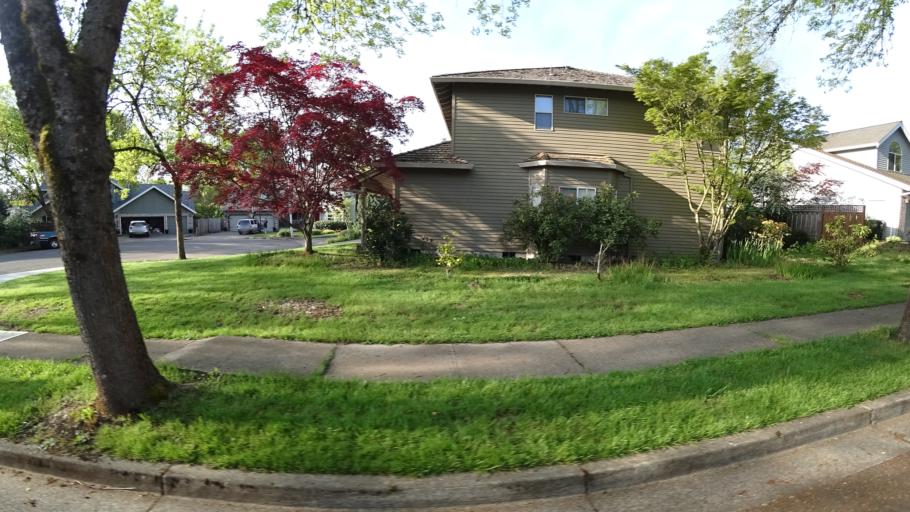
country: US
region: Oregon
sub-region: Washington County
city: Beaverton
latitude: 45.4454
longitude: -122.8218
